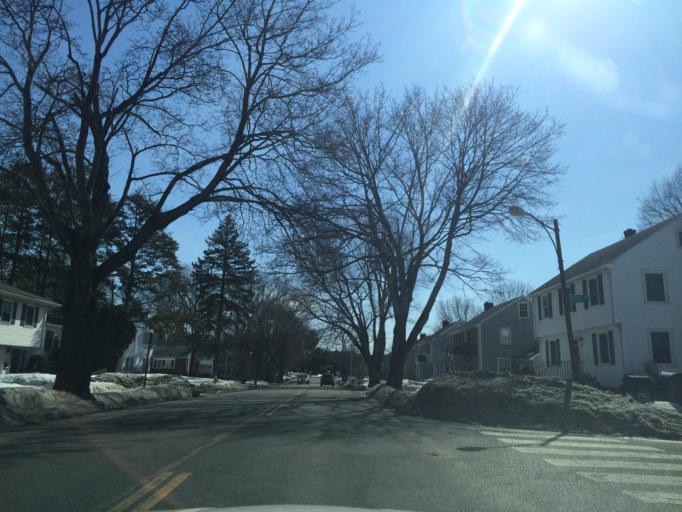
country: US
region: Massachusetts
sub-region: Middlesex County
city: Belmont
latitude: 42.3983
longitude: -71.1612
